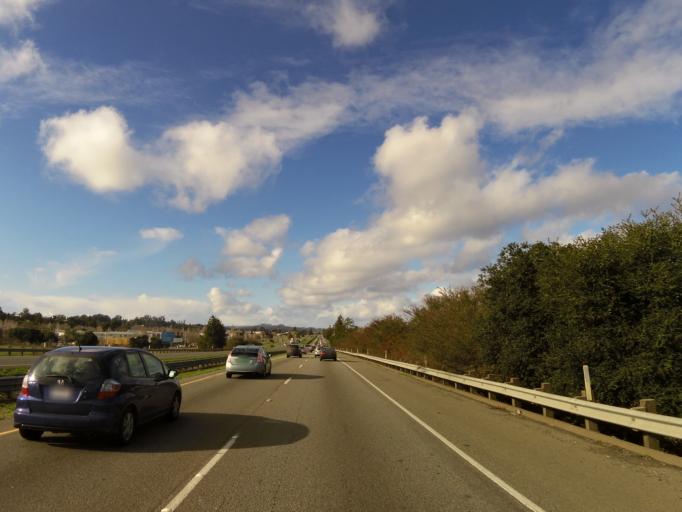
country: US
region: California
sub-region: Sonoma County
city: Petaluma
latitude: 38.2556
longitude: -122.6443
